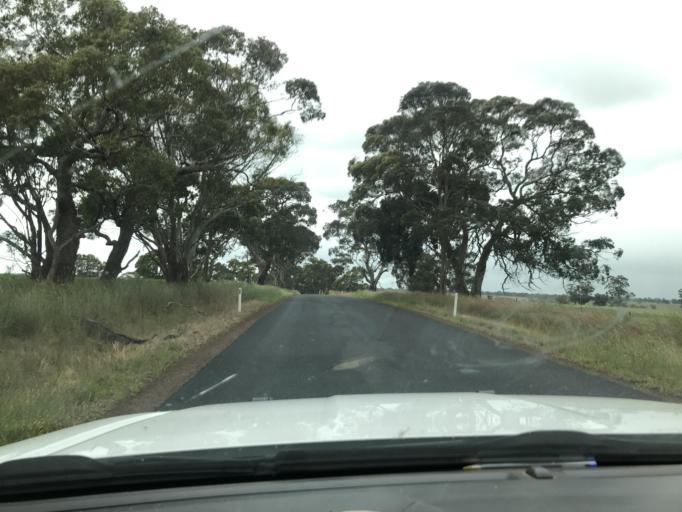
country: AU
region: Victoria
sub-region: Southern Grampians
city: Hamilton
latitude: -37.1820
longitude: 141.5661
